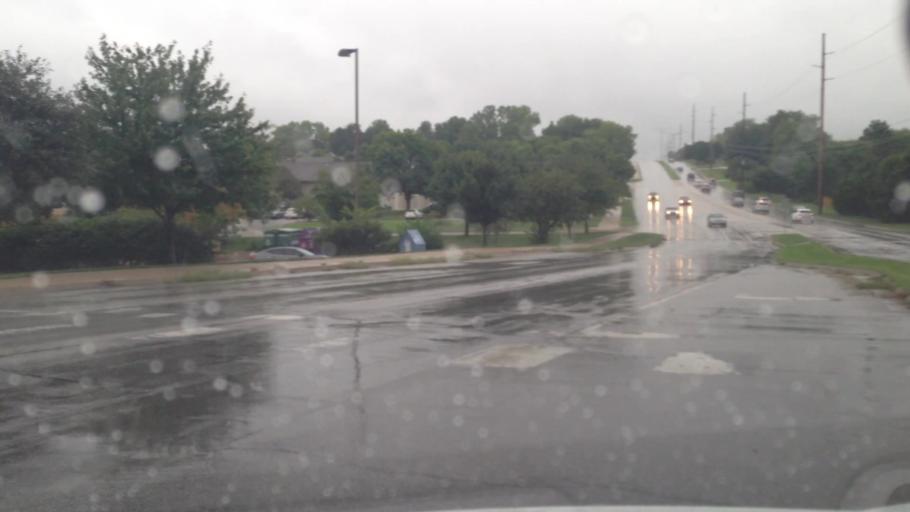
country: US
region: Kansas
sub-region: Douglas County
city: Lawrence
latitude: 38.9441
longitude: -95.2793
